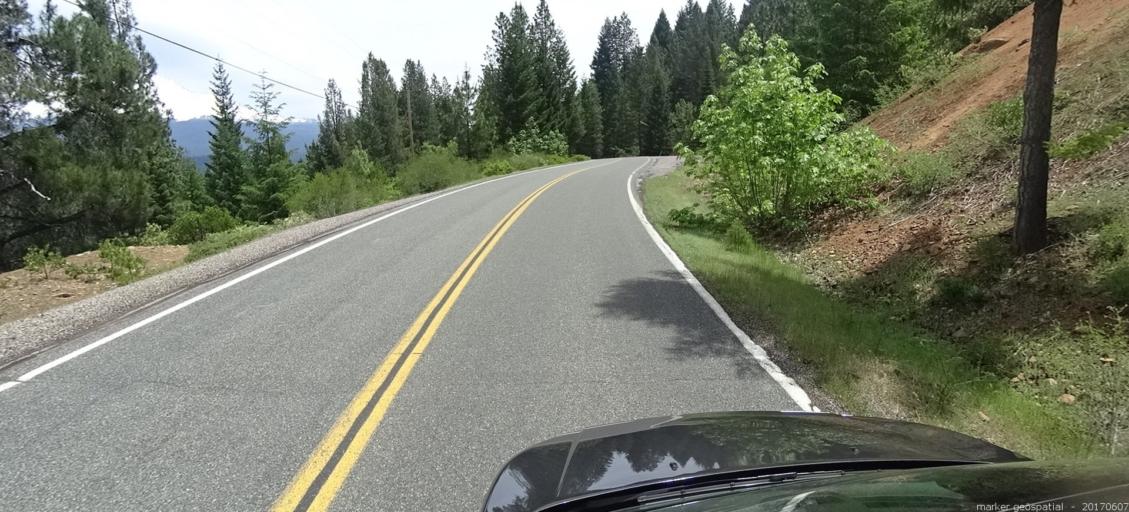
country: US
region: California
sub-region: Siskiyou County
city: Mount Shasta
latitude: 41.2715
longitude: -122.3469
